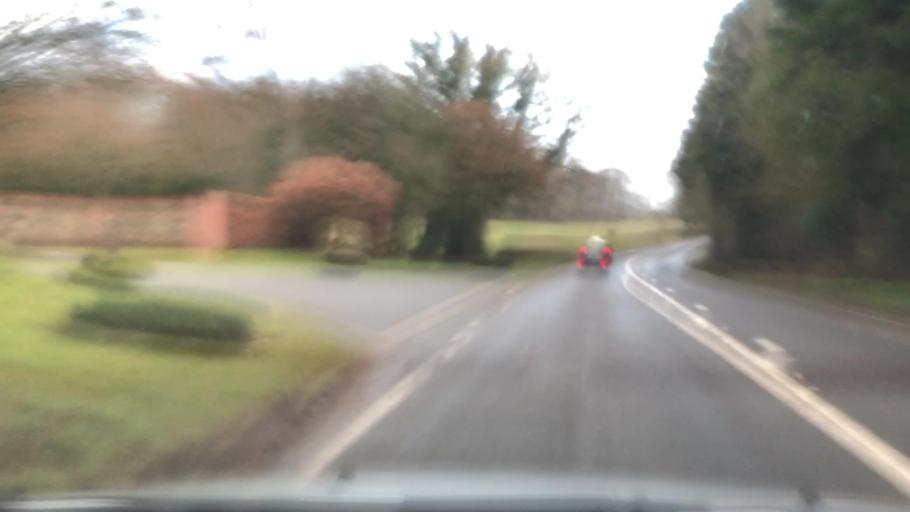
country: GB
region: England
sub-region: Hampshire
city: Alton
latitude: 51.1906
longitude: -0.9857
